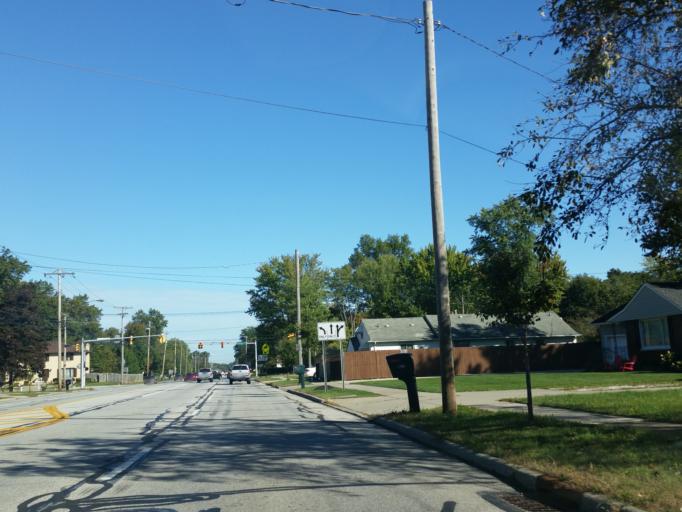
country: US
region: Ohio
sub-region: Cuyahoga County
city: Westlake
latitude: 41.4617
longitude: -81.9019
